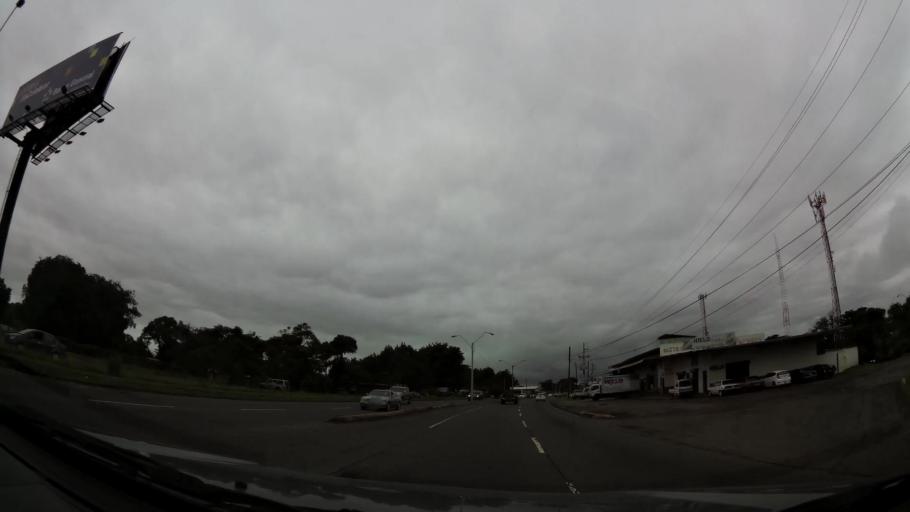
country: PA
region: Chiriqui
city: David
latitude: 8.4291
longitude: -82.4446
